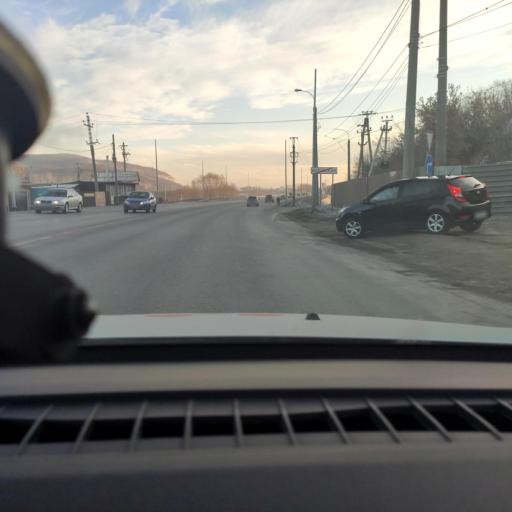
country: RU
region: Samara
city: Volzhskiy
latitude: 53.4240
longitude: 50.1252
